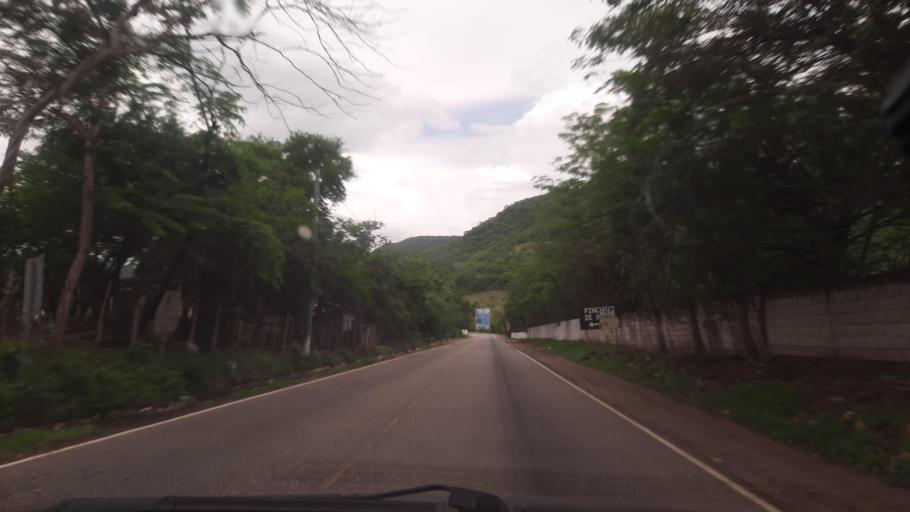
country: GT
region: Zacapa
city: San Jorge
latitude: 14.8968
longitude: -89.5218
